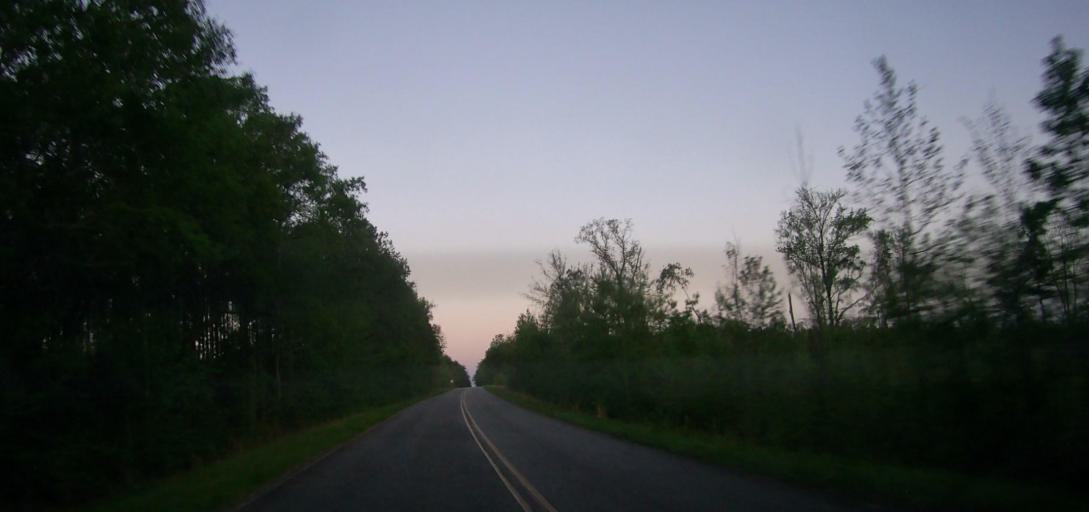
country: US
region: Georgia
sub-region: Marion County
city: Buena Vista
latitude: 32.2567
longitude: -84.5913
